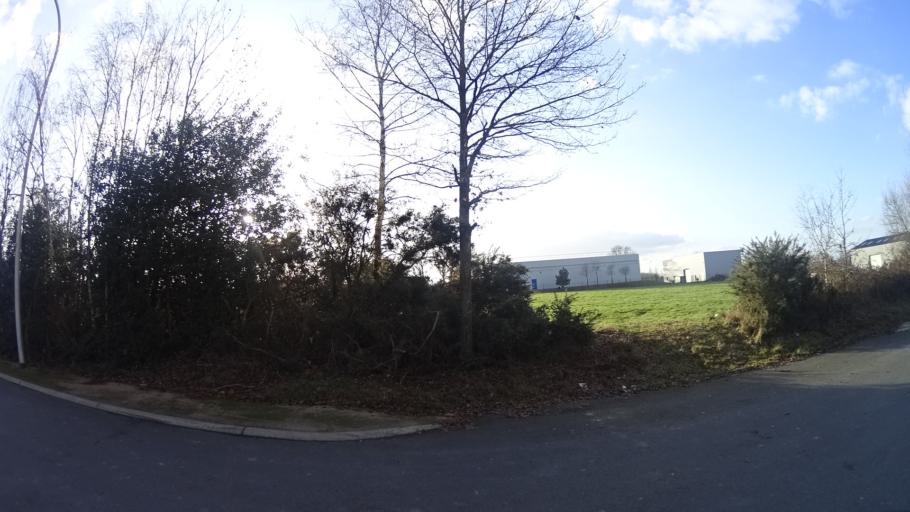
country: FR
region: Pays de la Loire
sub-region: Departement de la Loire-Atlantique
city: Saint-Nicolas-de-Redon
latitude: 47.6293
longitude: -2.0532
